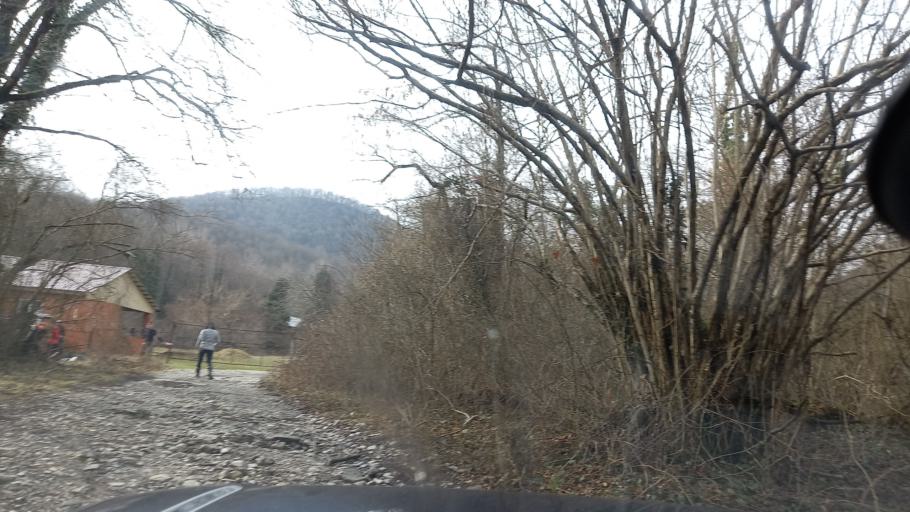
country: RU
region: Krasnodarskiy
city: Dzhubga
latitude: 44.4131
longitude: 38.7197
